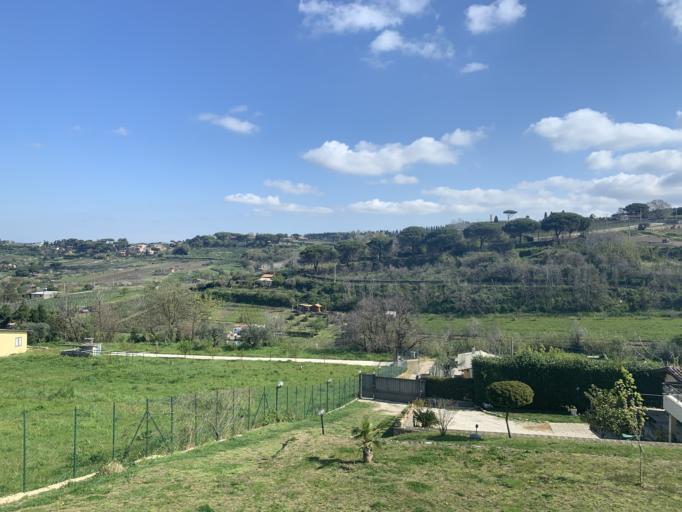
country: IT
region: Latium
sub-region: Citta metropolitana di Roma Capitale
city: Grottaferrata
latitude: 41.7844
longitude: 12.6496
